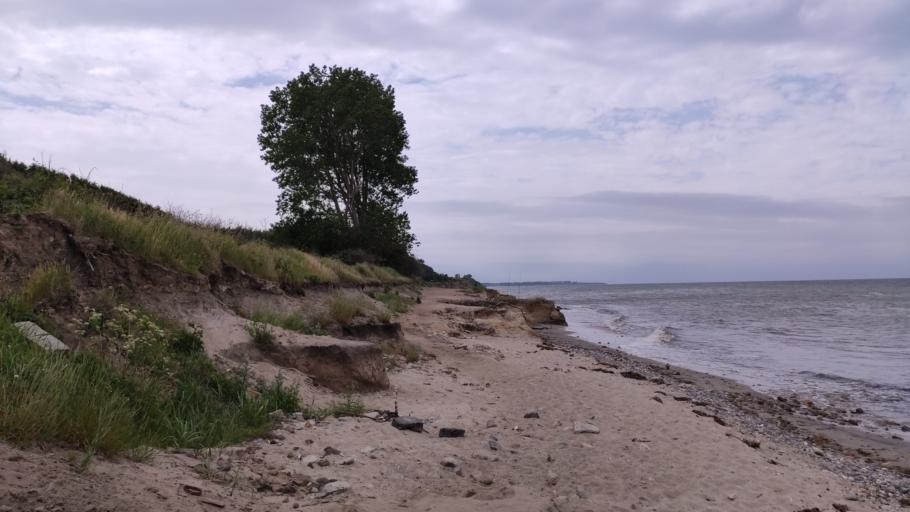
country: DE
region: Mecklenburg-Vorpommern
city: Bastorf
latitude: 54.1406
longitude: 11.6612
